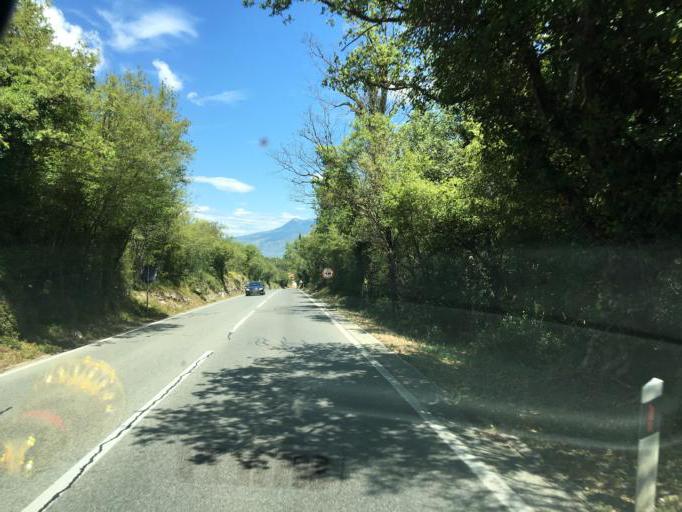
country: HR
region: Istarska
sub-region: Grad Labin
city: Labin
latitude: 45.1425
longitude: 14.1482
